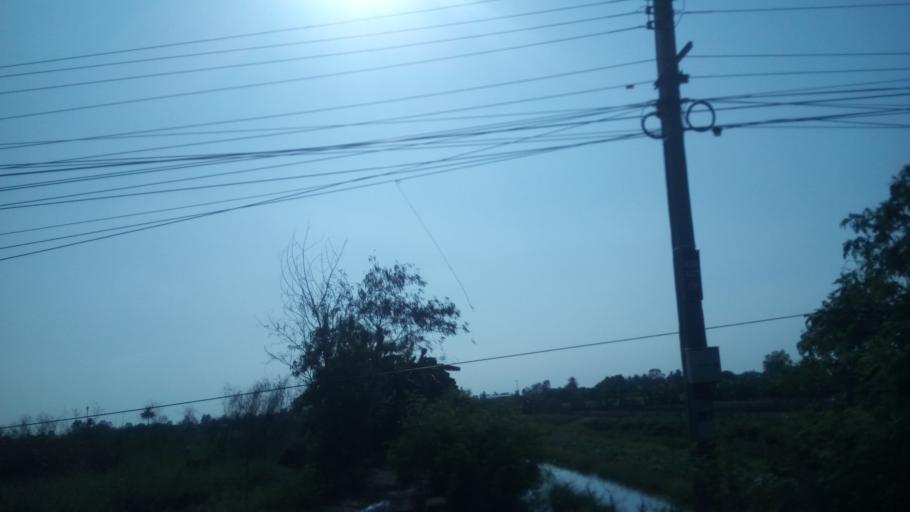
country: TH
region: Nonthaburi
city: Bang Yai
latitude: 13.8943
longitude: 100.3256
